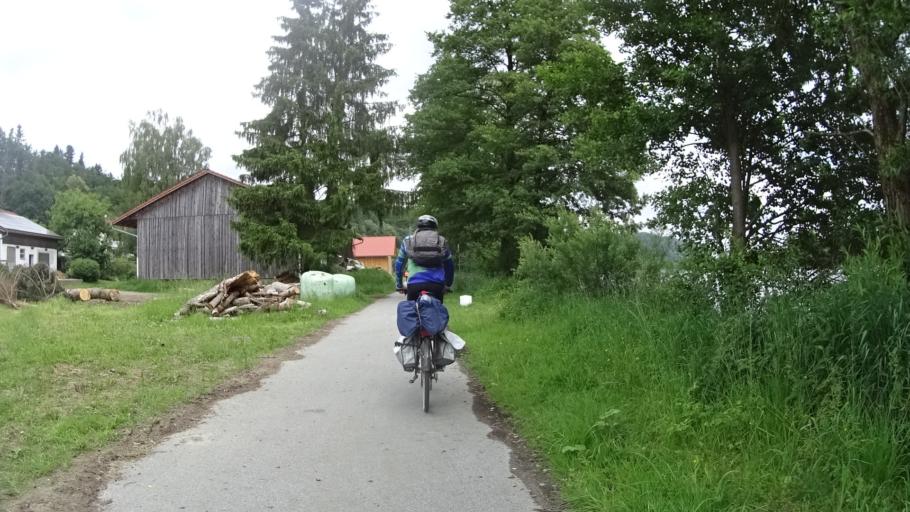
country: DE
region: Bavaria
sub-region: Lower Bavaria
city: Aicha vorm Wald
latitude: 48.6115
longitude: 13.2748
